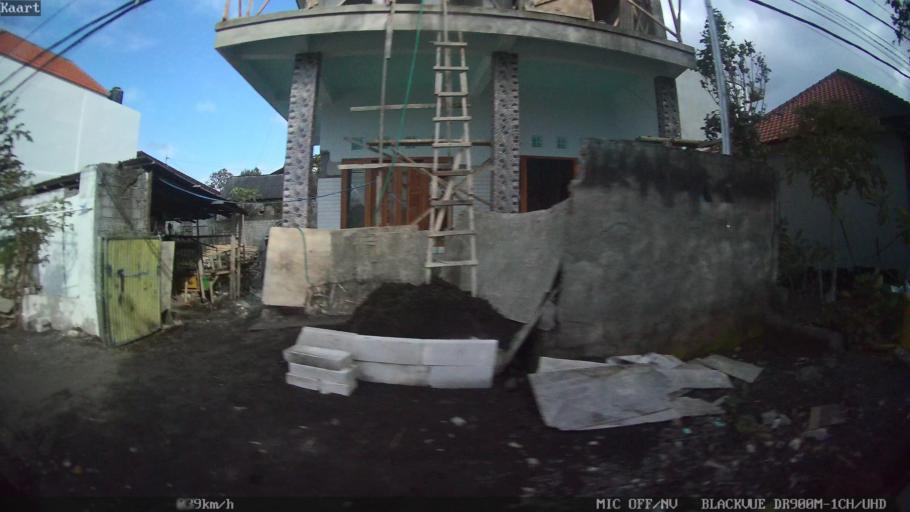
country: ID
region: Bali
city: Kuta
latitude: -8.7059
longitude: 115.1920
